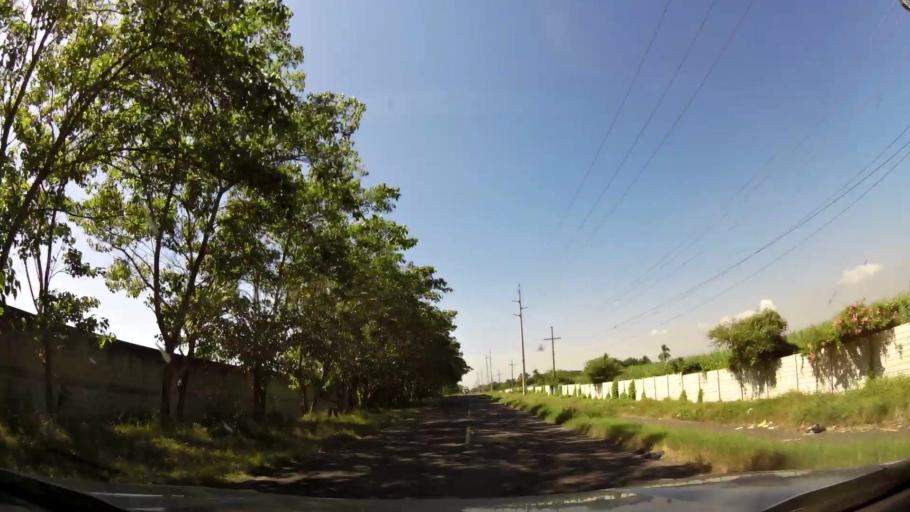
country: GT
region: Escuintla
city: Iztapa
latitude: 13.9344
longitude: -90.7561
